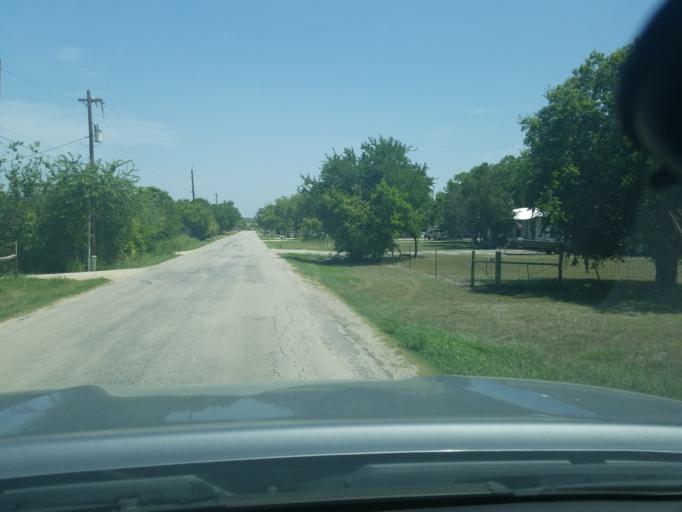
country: US
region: Texas
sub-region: Guadalupe County
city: Cibolo
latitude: 29.5743
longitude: -98.1943
